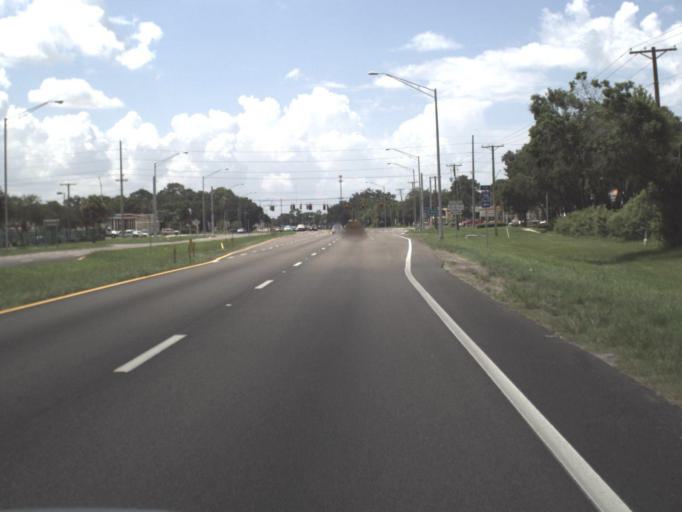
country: US
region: Florida
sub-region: Hillsborough County
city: East Lake-Orient Park
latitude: 27.9837
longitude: -82.3598
